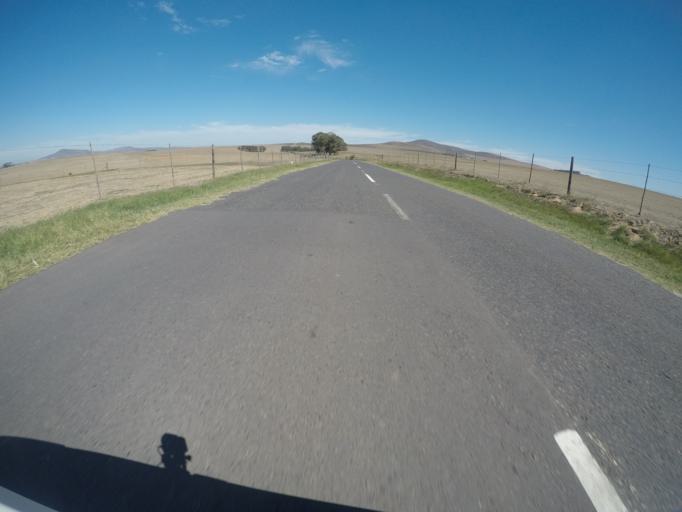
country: ZA
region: Western Cape
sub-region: City of Cape Town
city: Atlantis
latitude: -33.6907
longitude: 18.5946
